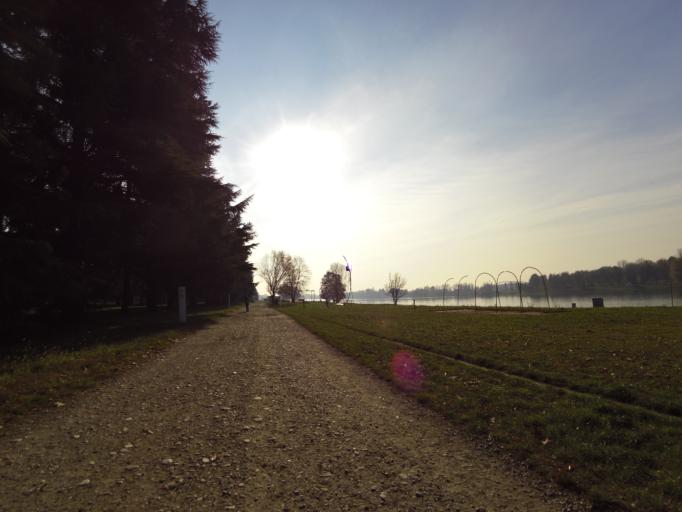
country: IT
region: Lombardy
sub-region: Citta metropolitana di Milano
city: Novegro-Tregarezzo-San Felice
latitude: 45.4661
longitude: 9.2916
